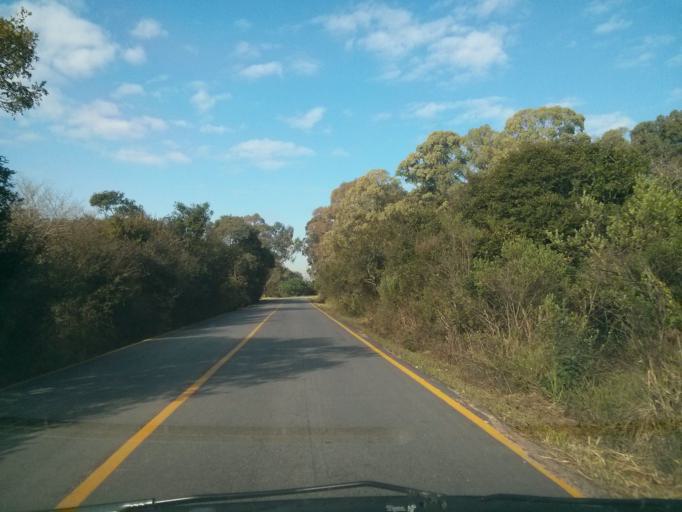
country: BR
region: Parana
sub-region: Sao Jose Dos Pinhais
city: Sao Jose dos Pinhais
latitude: -25.5357
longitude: -49.2259
